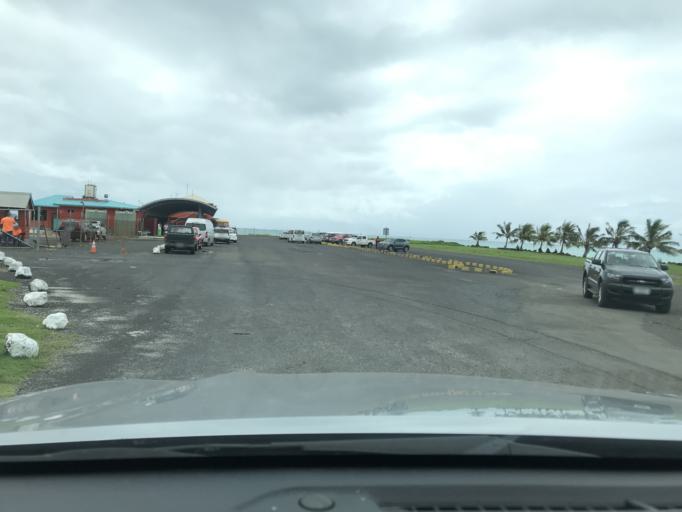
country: WS
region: Aiga-i-le-Tai
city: Mulifanua
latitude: -13.8304
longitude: -172.0351
